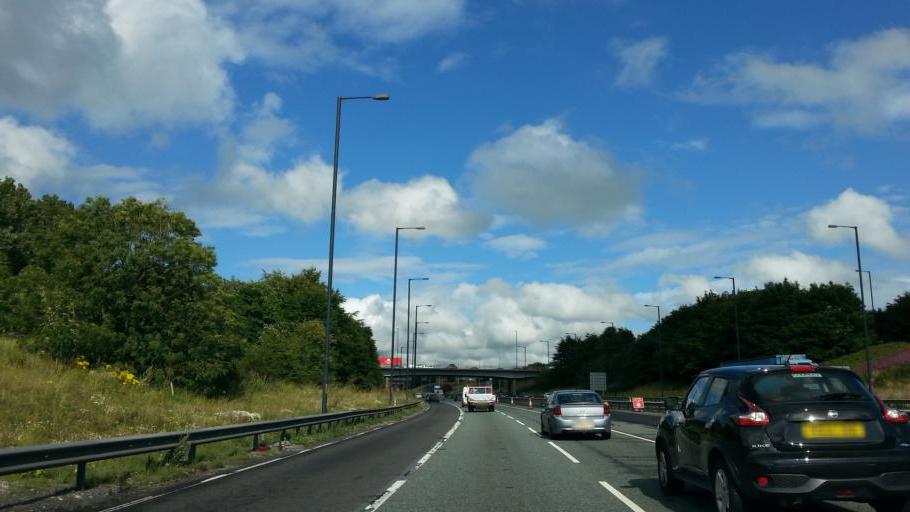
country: GB
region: England
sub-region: Borough of Rochdale
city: Rochdale
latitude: 53.5860
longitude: -2.1629
